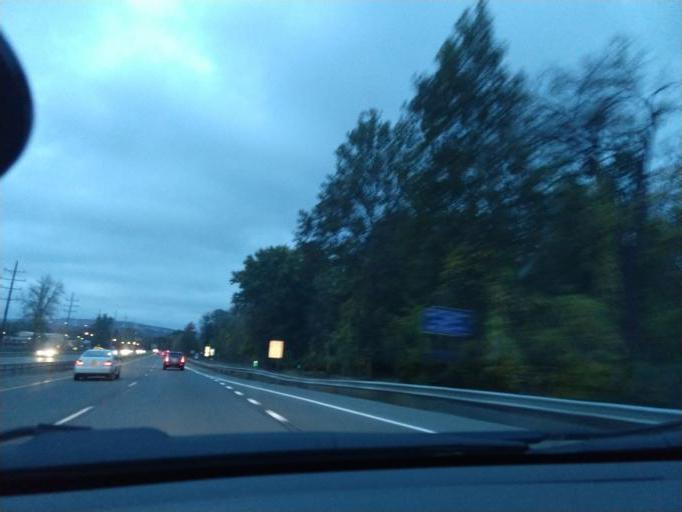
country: US
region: New York
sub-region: Tompkins County
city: Cayuga Heights
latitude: 42.4598
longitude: -76.5007
